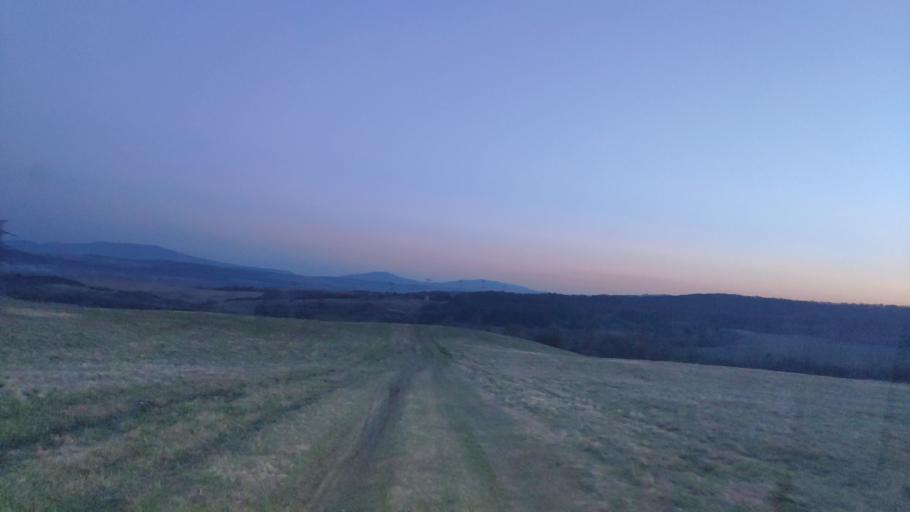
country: SK
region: Kosicky
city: Kosice
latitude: 48.8286
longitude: 21.2620
